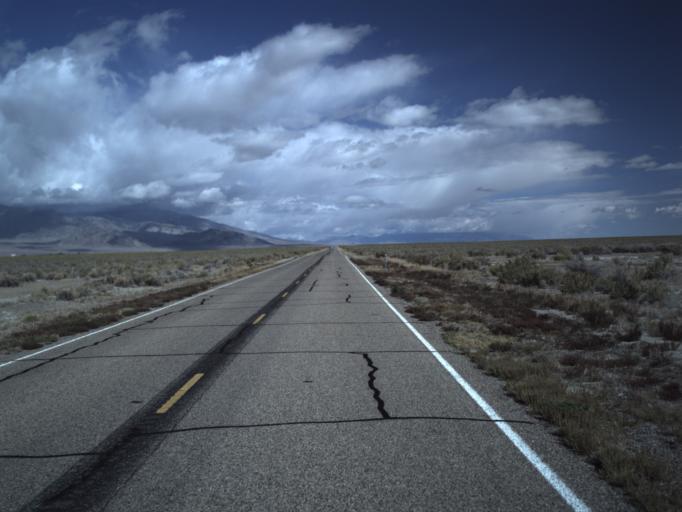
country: US
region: Nevada
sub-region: White Pine County
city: McGill
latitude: 39.0241
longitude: -114.0355
